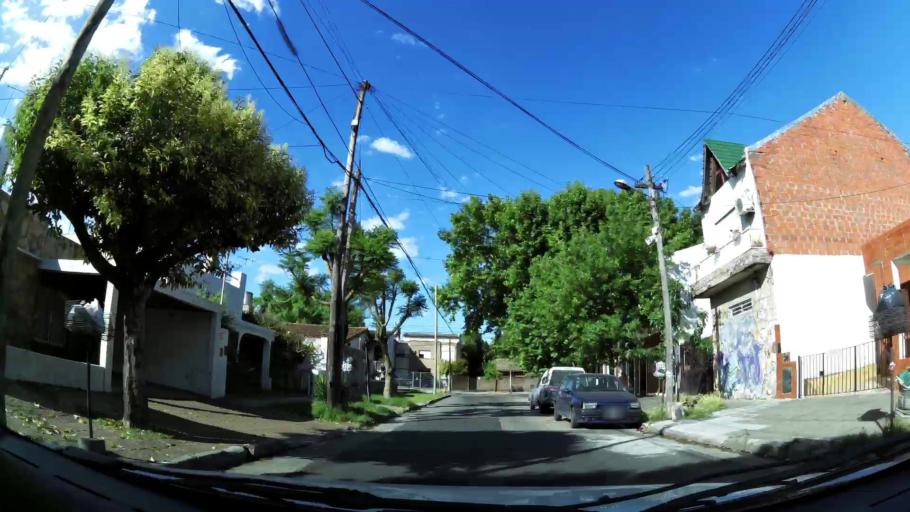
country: AR
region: Buenos Aires
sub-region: Partido de General San Martin
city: General San Martin
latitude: -34.5415
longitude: -58.5558
